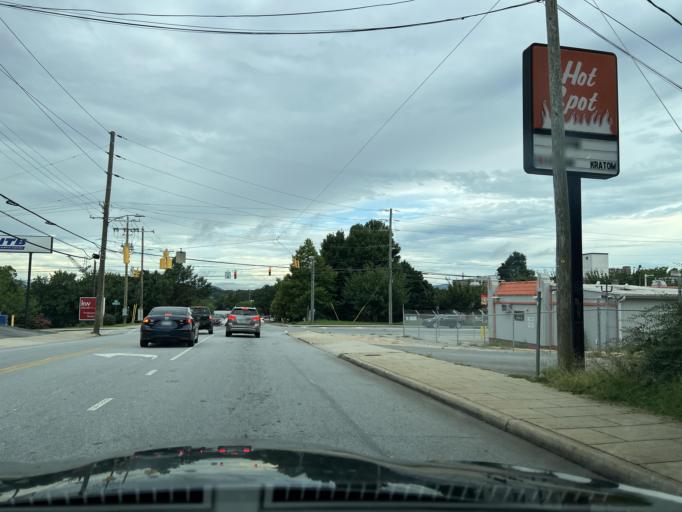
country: US
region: North Carolina
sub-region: Buncombe County
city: Asheville
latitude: 35.5917
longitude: -82.5565
